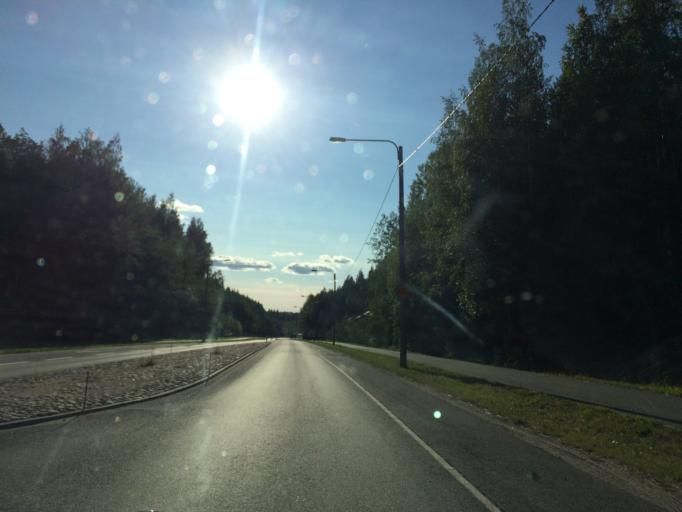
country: FI
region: Haeme
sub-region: Haemeenlinna
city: Haemeenlinna
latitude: 60.9820
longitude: 24.5183
